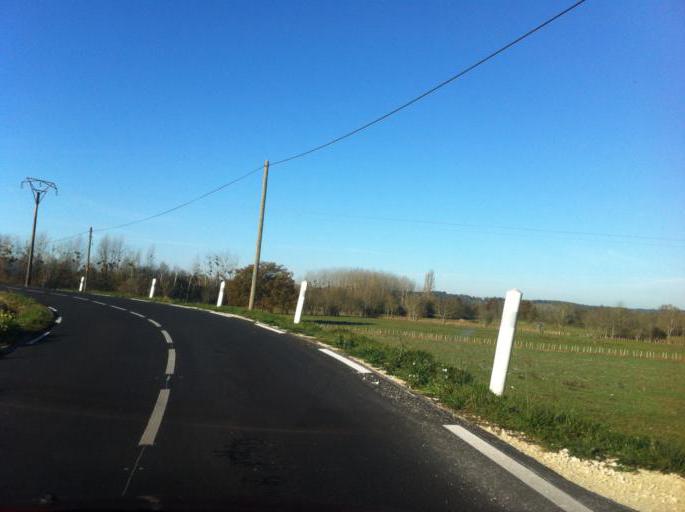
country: FR
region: Aquitaine
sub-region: Departement de la Dordogne
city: Riberac
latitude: 45.2720
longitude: 0.2426
